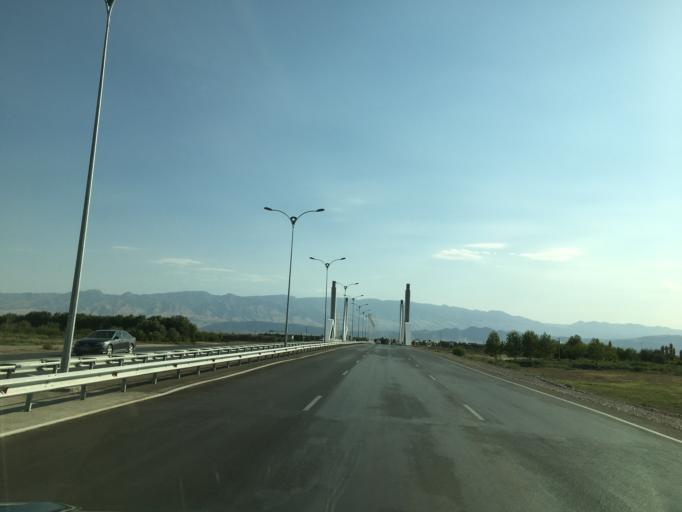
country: TM
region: Ahal
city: Abadan
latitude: 38.0493
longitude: 58.2976
